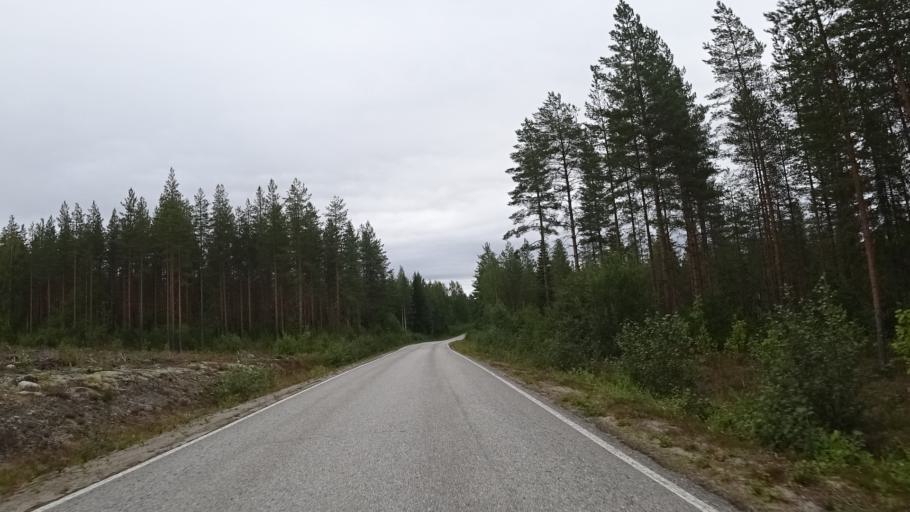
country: FI
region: North Karelia
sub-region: Pielisen Karjala
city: Lieksa
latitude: 63.3677
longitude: 30.2915
